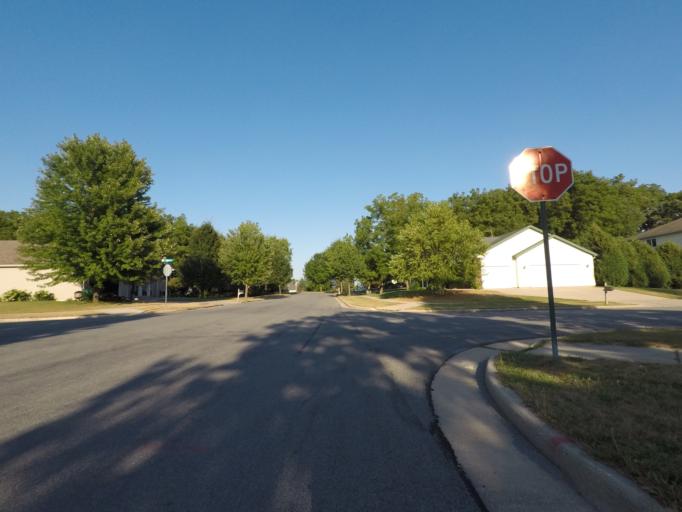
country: US
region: Wisconsin
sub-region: Dane County
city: Verona
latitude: 43.0055
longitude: -89.5394
